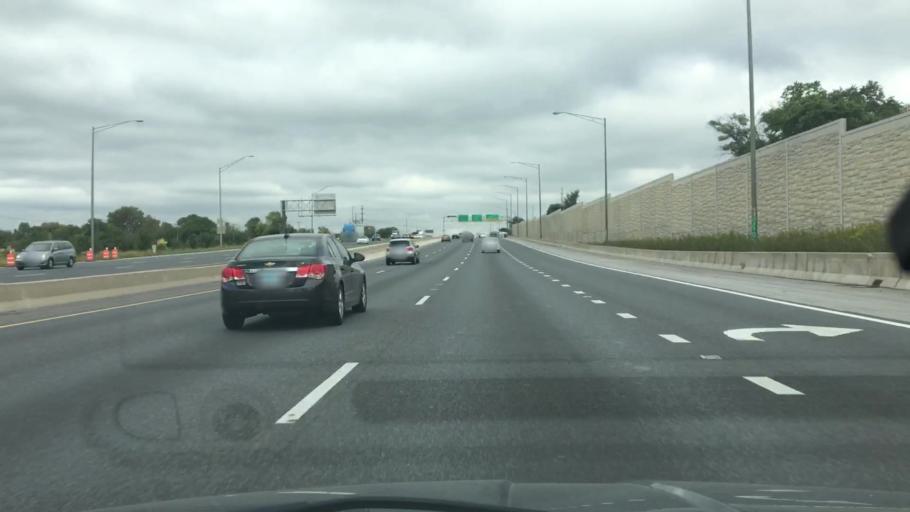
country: US
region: Illinois
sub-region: Cook County
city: Lemont
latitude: 41.7130
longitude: -88.0140
